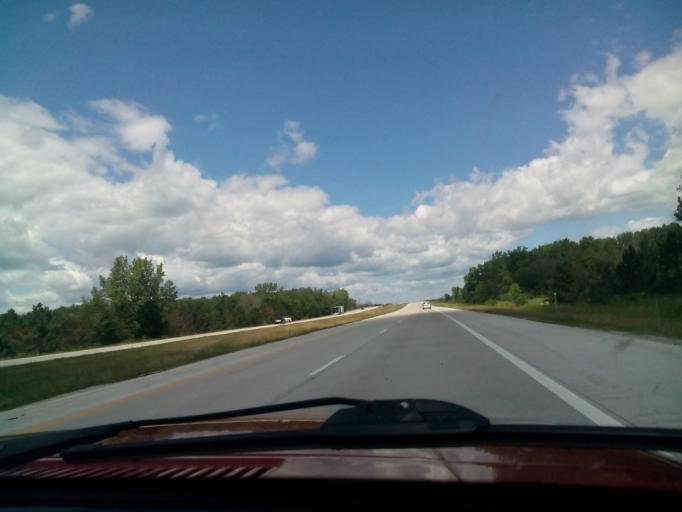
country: US
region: Michigan
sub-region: Bay County
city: Pinconning
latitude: 43.8911
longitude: -84.0197
